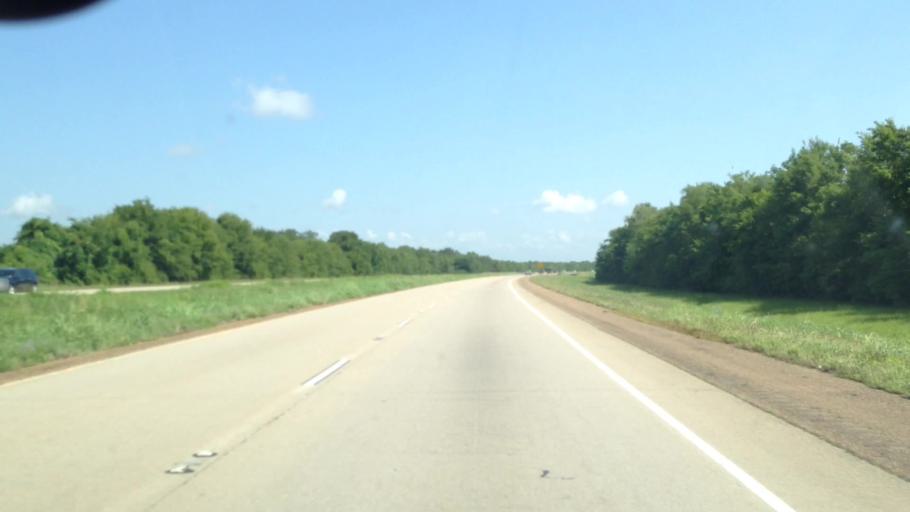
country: US
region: Louisiana
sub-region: Rapides Parish
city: Woodworth
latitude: 31.1933
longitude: -92.4738
